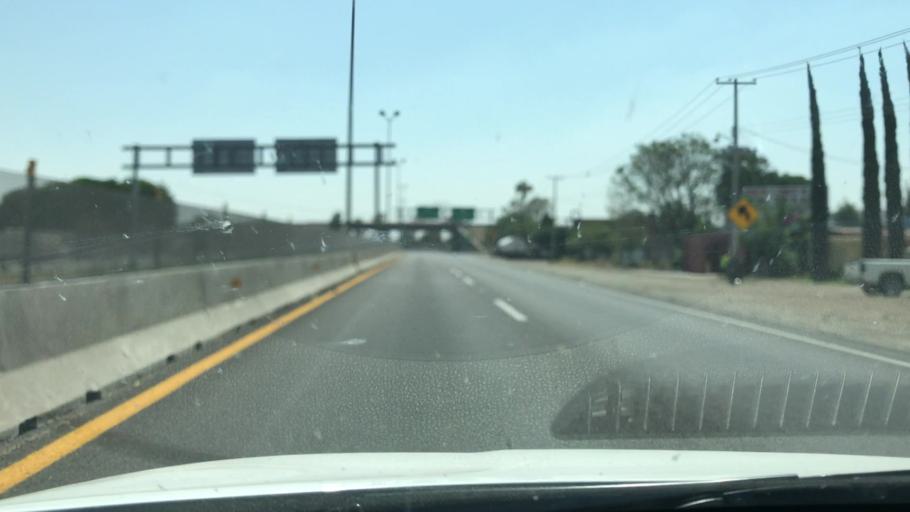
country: MX
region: Guanajuato
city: Abasolo
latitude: 20.4655
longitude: -101.5114
